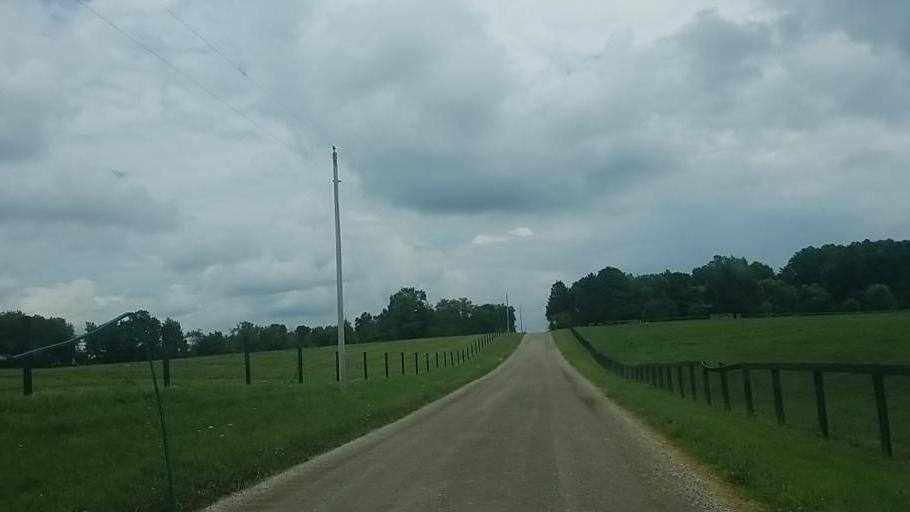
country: US
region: Ohio
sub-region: Licking County
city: Utica
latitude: 40.2189
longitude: -82.3554
